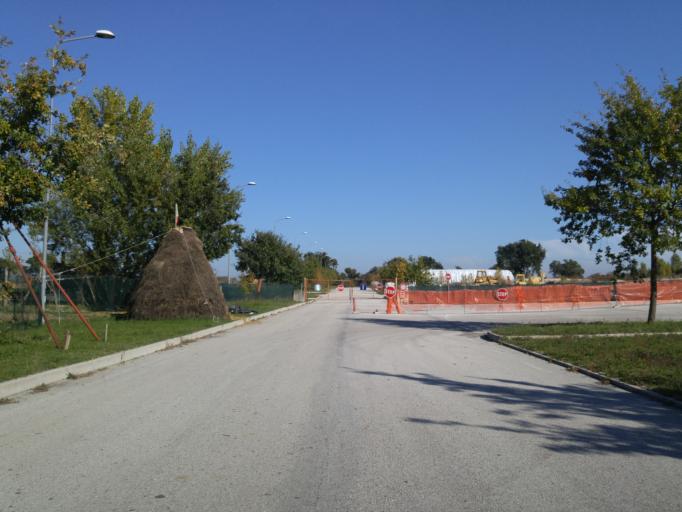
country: IT
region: The Marches
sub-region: Provincia di Pesaro e Urbino
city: Tavernelle
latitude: 43.7246
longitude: 12.8944
